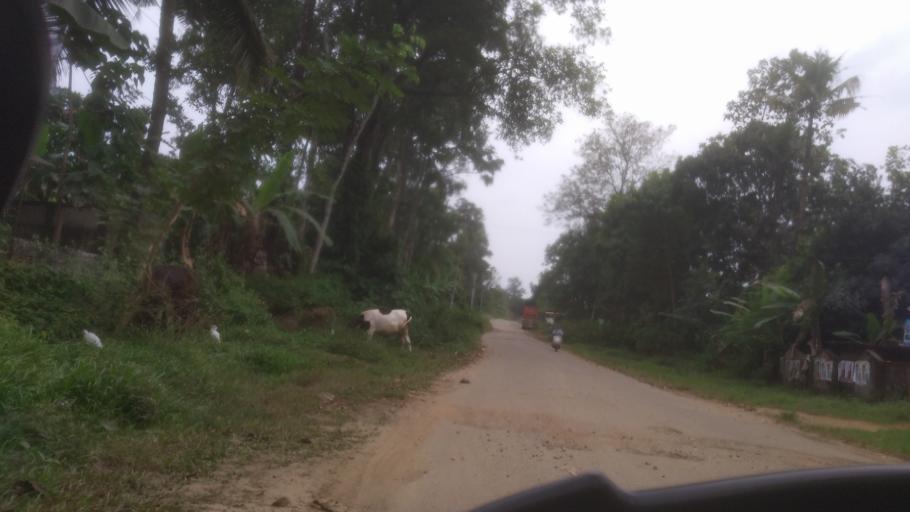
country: IN
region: Kerala
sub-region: Ernakulam
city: Perumbavoor
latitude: 10.0516
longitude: 76.5221
